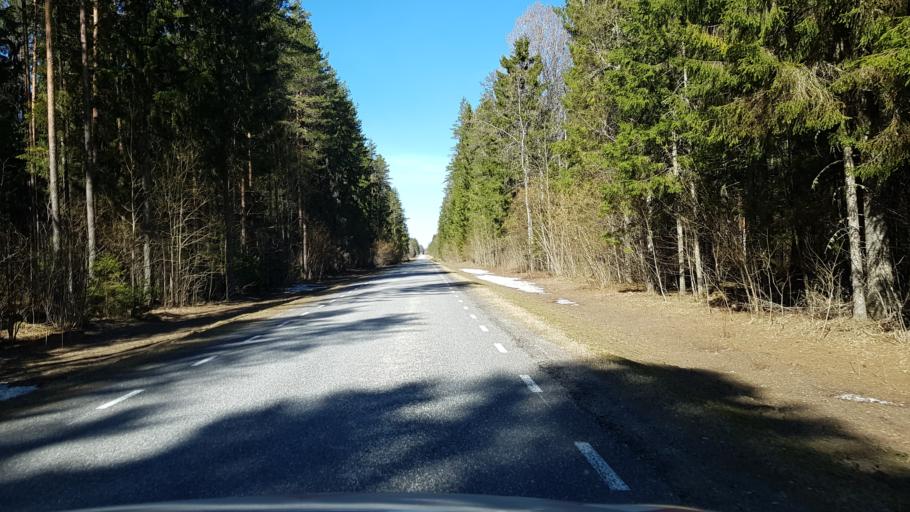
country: EE
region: Laeaene-Virumaa
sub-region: Vinni vald
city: Vinni
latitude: 59.1527
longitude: 26.5175
